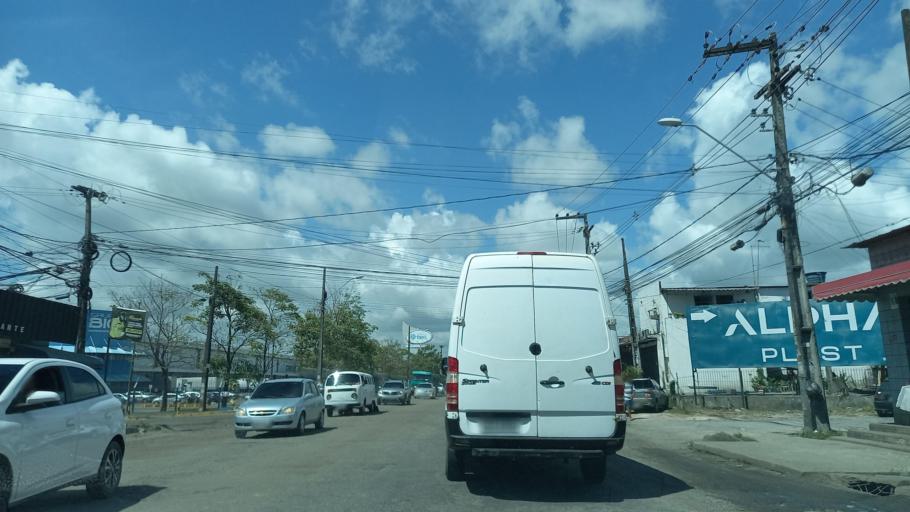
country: BR
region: Pernambuco
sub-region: Jaboatao Dos Guararapes
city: Jaboatao
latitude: -8.1549
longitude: -34.9452
